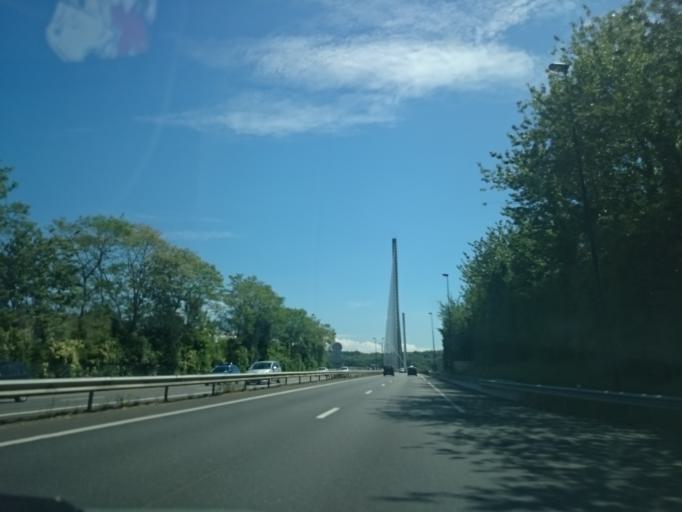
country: FR
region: Brittany
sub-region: Departement du Finistere
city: Le Relecq-Kerhuon
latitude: 48.3921
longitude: -4.4031
